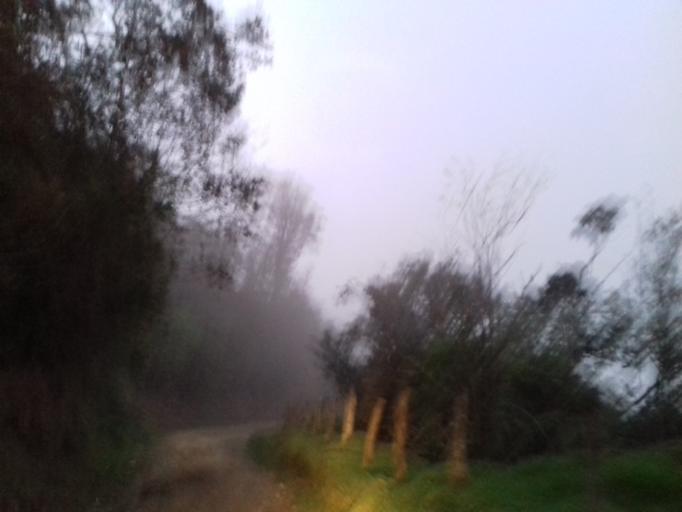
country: CO
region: Quindio
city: Salento
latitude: 4.5784
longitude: -75.5258
